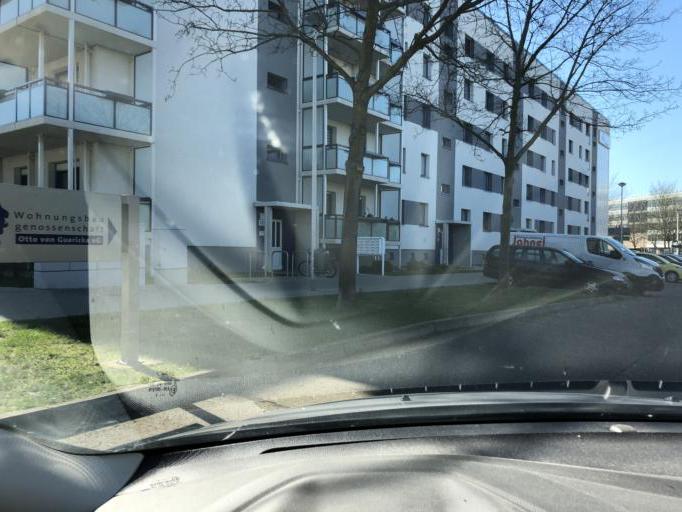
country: DE
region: Saxony-Anhalt
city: Diesdorf
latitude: 52.1487
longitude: 11.5848
